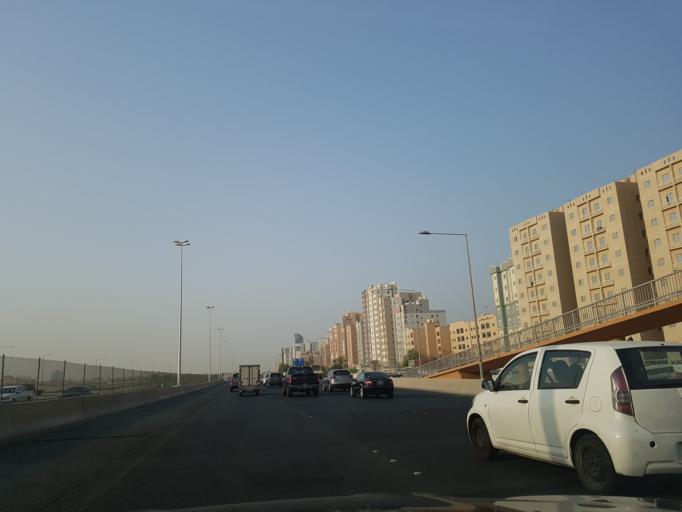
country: KW
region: Al Ahmadi
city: Al Mahbulah
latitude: 29.1474
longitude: 48.1128
